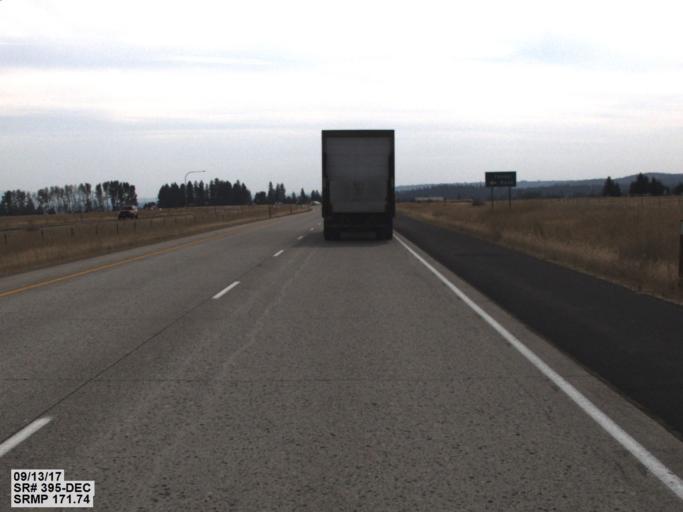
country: US
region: Washington
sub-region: Spokane County
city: Fairwood
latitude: 47.8411
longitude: -117.4223
